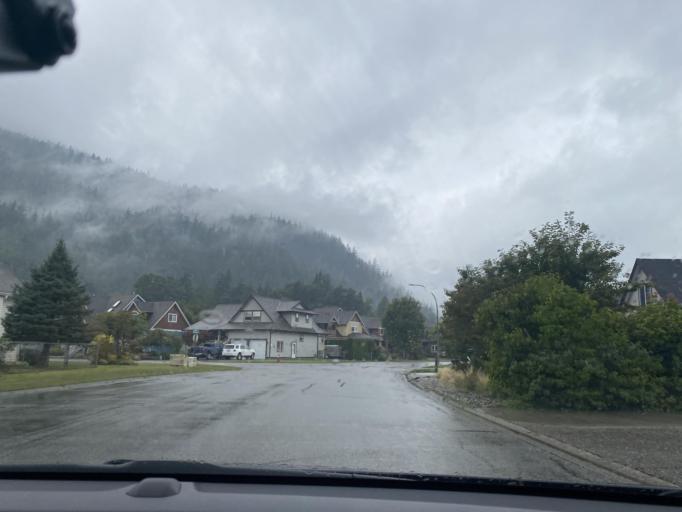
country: CA
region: British Columbia
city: Agassiz
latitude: 49.2969
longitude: -121.7793
